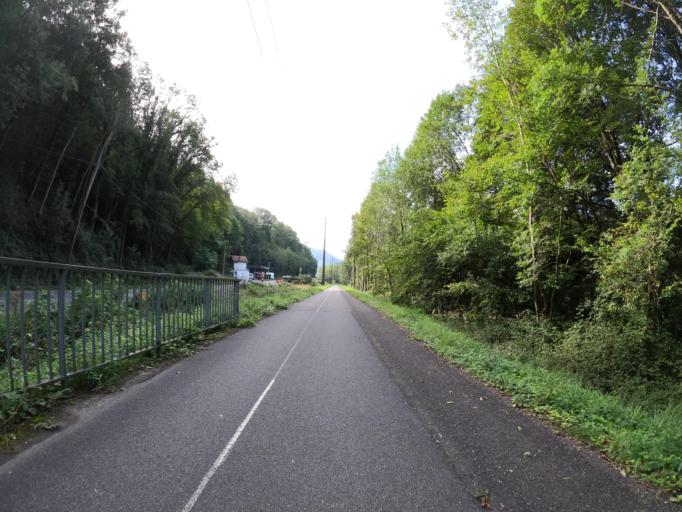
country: FR
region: Midi-Pyrenees
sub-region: Departement des Hautes-Pyrenees
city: Lourdes
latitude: 43.0723
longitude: -0.0402
